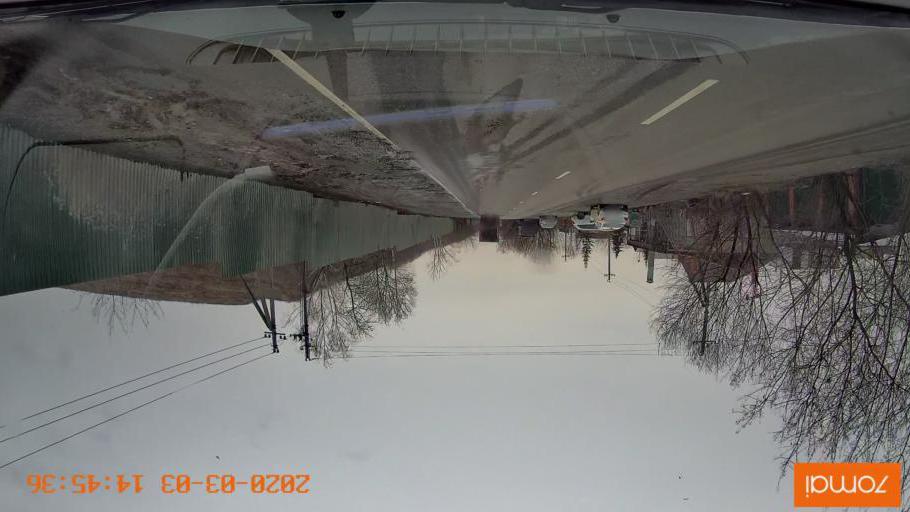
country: RU
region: Moskovskaya
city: Korenevo
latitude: 55.6992
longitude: 38.0483
